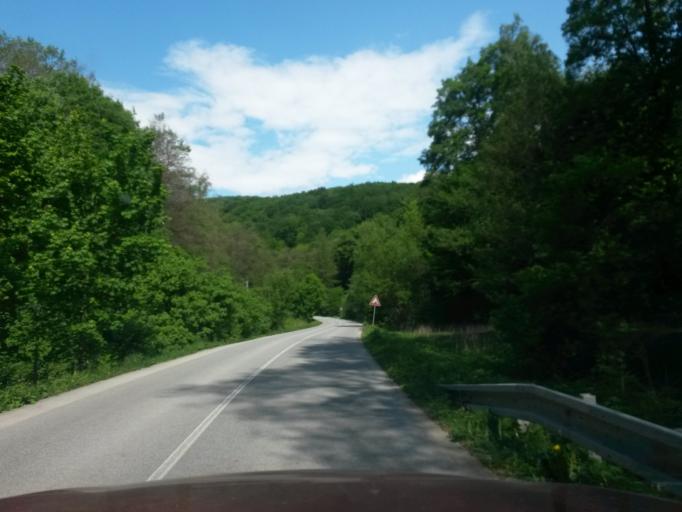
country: SK
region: Kosicky
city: Moldava nad Bodvou
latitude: 48.7259
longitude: 21.0683
